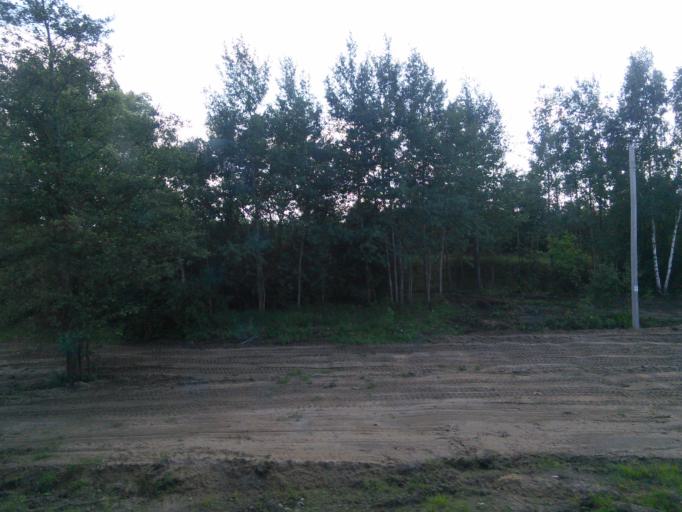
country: BY
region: Minsk
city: Maladzyechna
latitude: 54.2890
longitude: 26.9304
